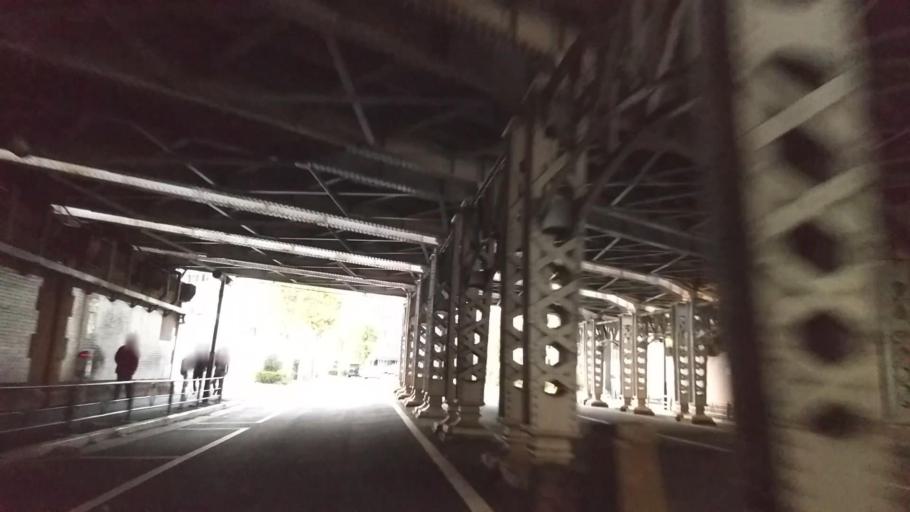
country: JP
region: Tokyo
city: Tokyo
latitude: 35.6880
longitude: 139.7695
